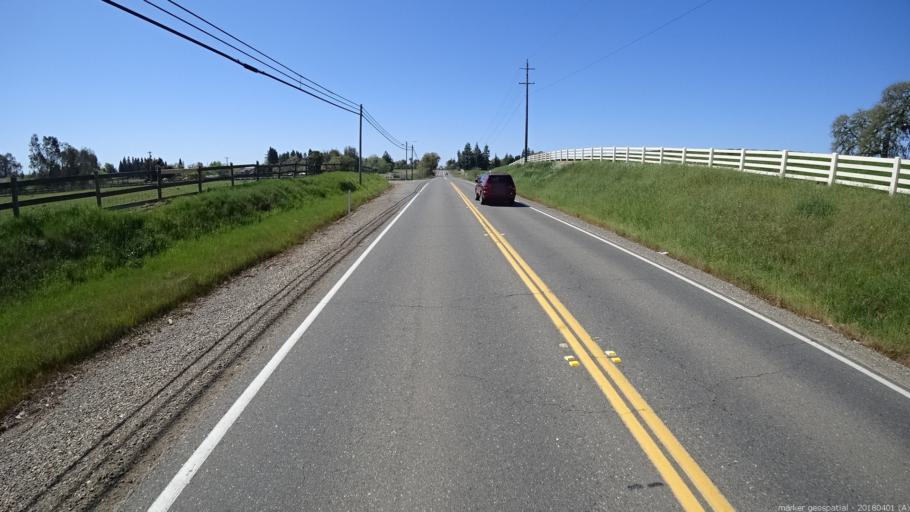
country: US
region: California
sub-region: Sacramento County
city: Wilton
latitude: 38.4186
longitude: -121.2242
